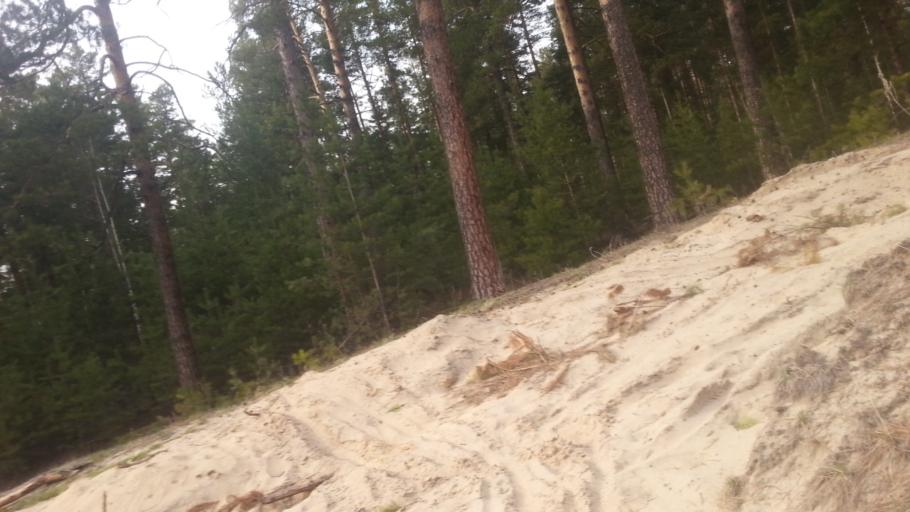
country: RU
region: Altai Krai
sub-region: Gorod Barnaulskiy
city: Barnaul
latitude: 53.3249
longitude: 83.7145
